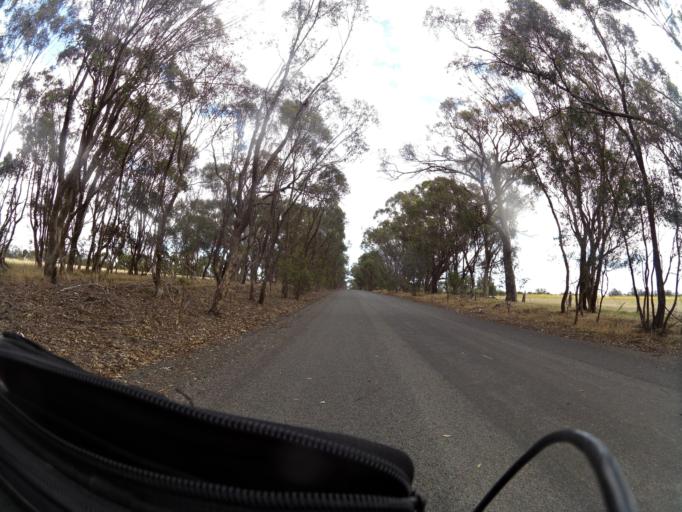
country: AU
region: Victoria
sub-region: Greater Shepparton
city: Shepparton
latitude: -36.7310
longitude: 145.1545
